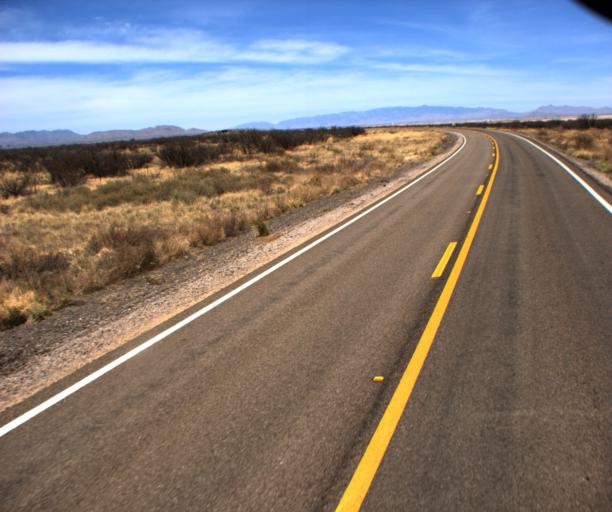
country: US
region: Arizona
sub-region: Cochise County
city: Willcox
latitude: 32.1259
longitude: -109.9087
